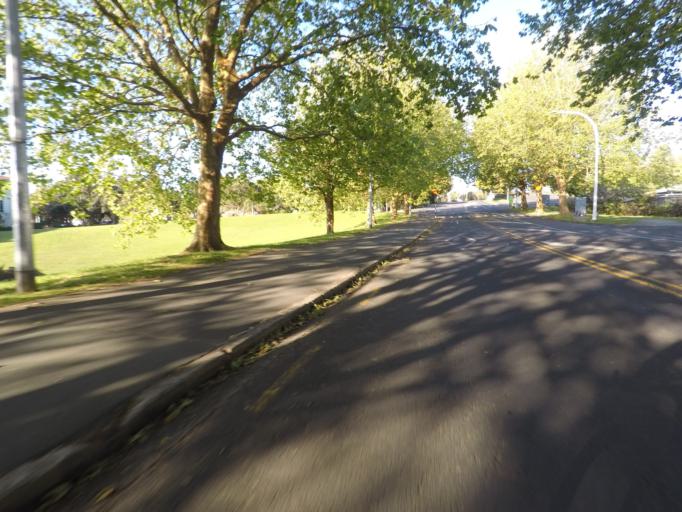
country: NZ
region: Auckland
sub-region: Auckland
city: Rosebank
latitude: -36.8807
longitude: 174.7098
